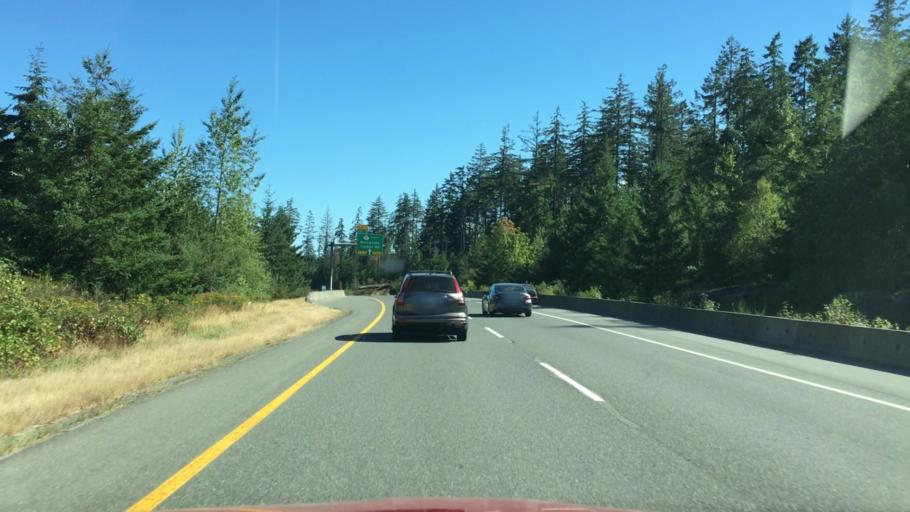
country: CA
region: British Columbia
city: Nanaimo
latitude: 49.1288
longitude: -123.9301
